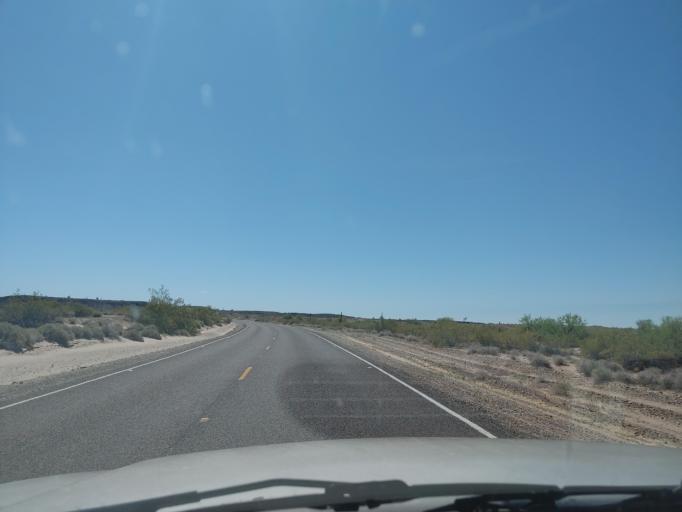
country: US
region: Arizona
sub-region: Maricopa County
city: Gila Bend
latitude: 32.9403
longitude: -113.3055
